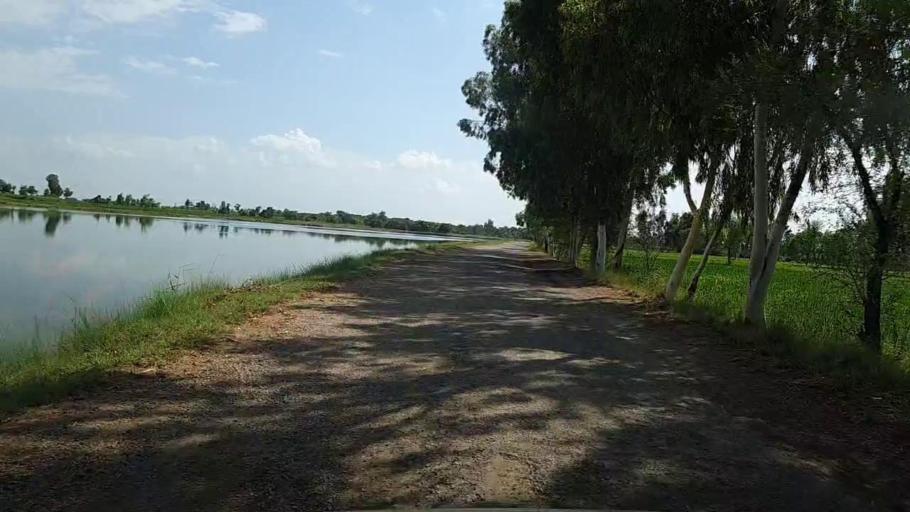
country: PK
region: Sindh
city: Bhiria
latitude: 26.9139
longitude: 68.2283
